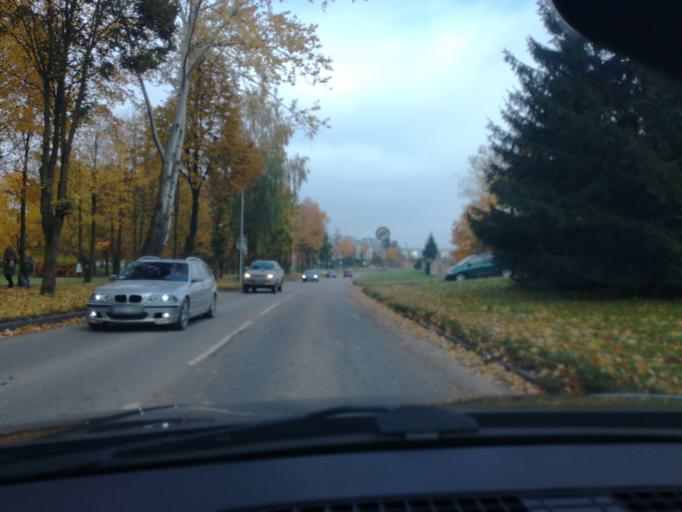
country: LT
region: Alytaus apskritis
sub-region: Alytus
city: Alytus
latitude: 54.3920
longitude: 24.0316
